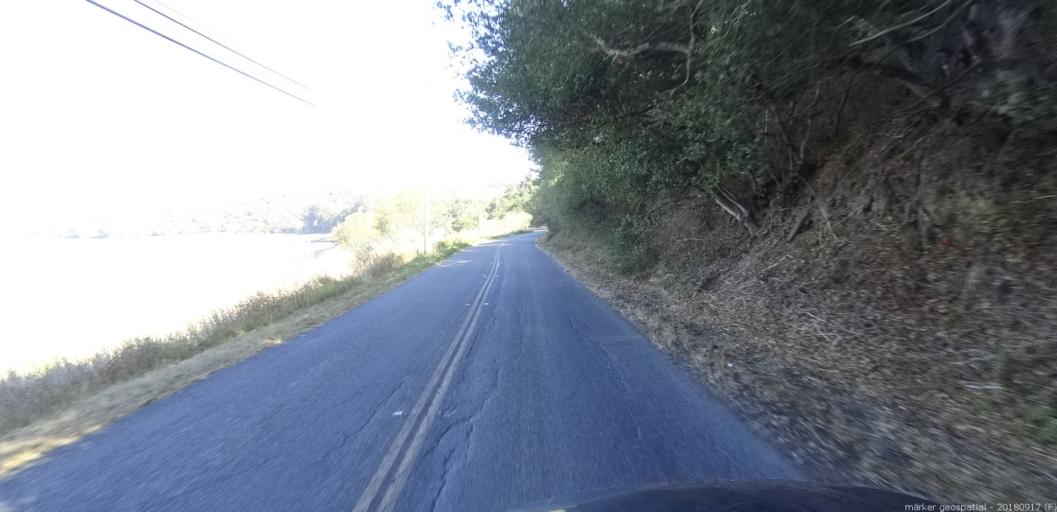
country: US
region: California
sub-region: Monterey County
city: Elkhorn
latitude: 36.8325
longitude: -121.7334
